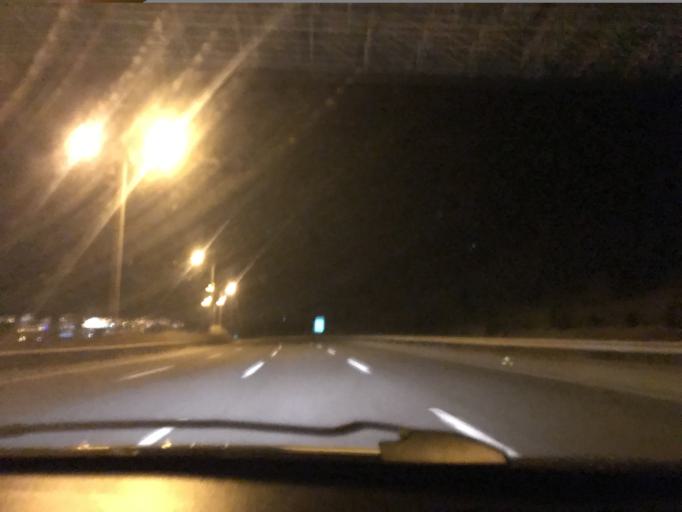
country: TR
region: Ankara
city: Etimesgut
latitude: 39.8513
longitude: 32.6268
